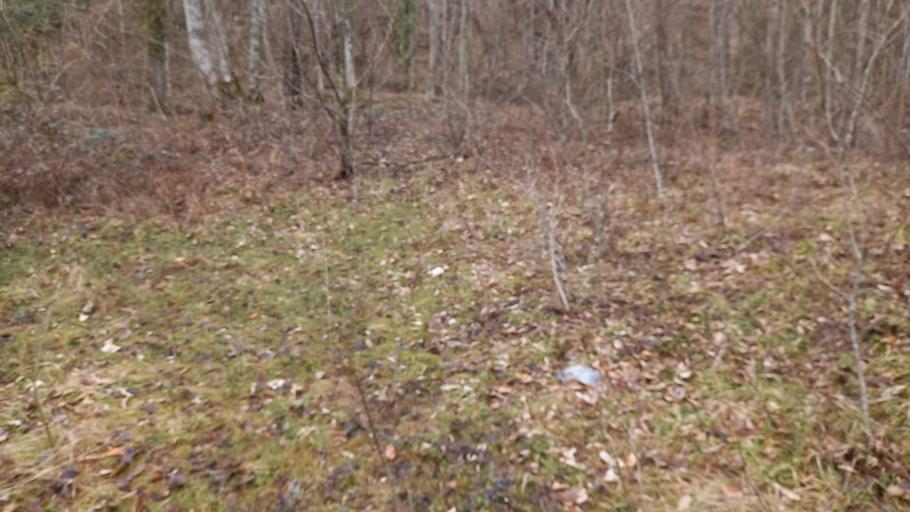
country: RU
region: Krasnodarskiy
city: Pshada
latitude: 44.4917
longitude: 38.3899
